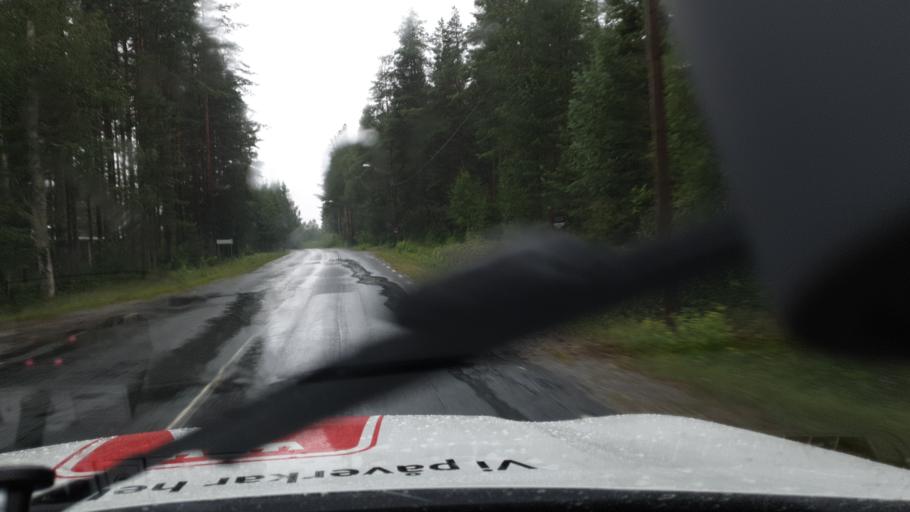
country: SE
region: Vaesterbotten
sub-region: Skelleftea Kommun
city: Soedra Bergsbyn
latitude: 64.5811
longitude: 21.0102
